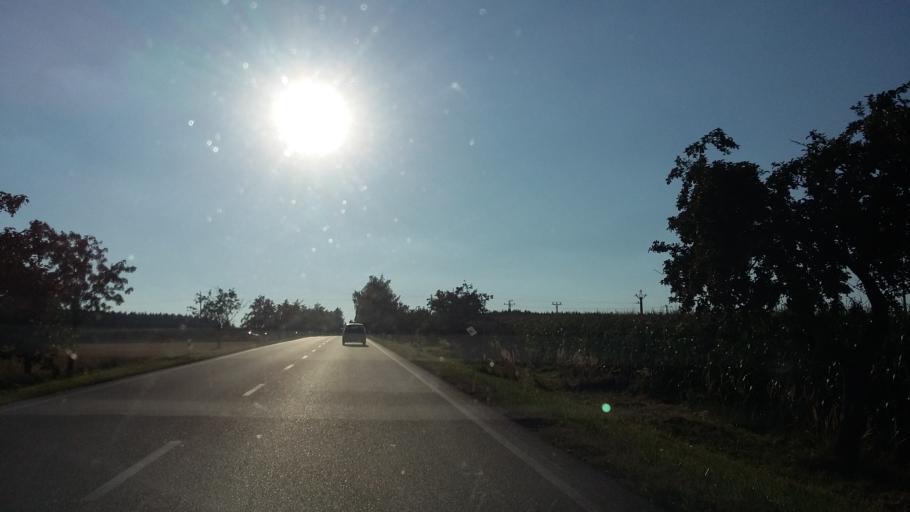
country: CZ
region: Vysocina
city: Merin
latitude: 49.4007
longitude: 15.8299
